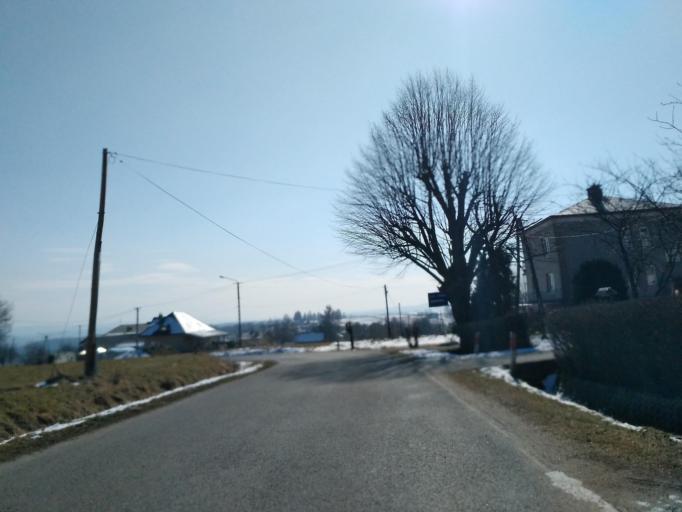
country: PL
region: Subcarpathian Voivodeship
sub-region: Powiat brzozowski
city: Jasienica Rosielna
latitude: 49.7664
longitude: 21.9239
